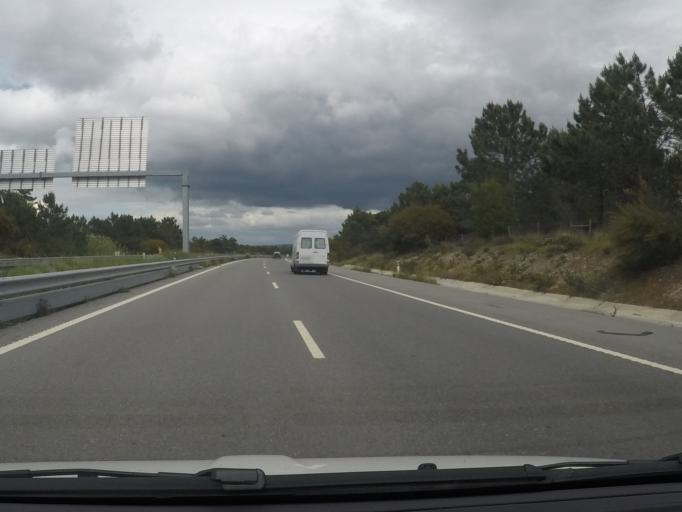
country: PT
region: Setubal
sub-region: Sines
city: Sines
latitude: 37.9769
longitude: -8.8023
